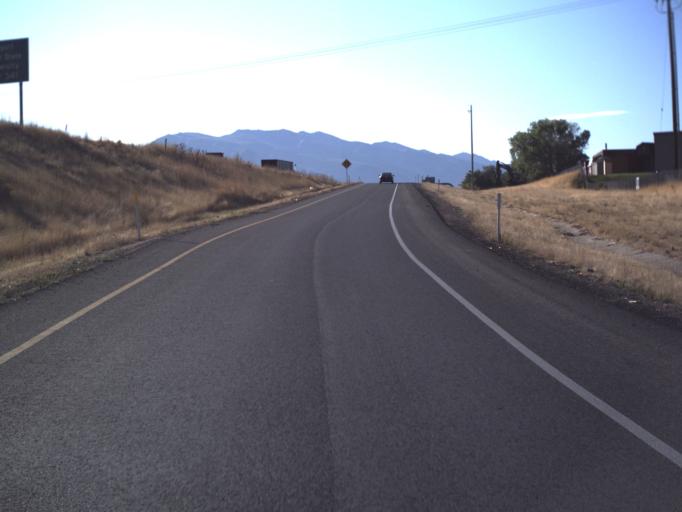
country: US
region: Utah
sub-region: Weber County
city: Ogden
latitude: 41.2181
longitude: -112.0044
